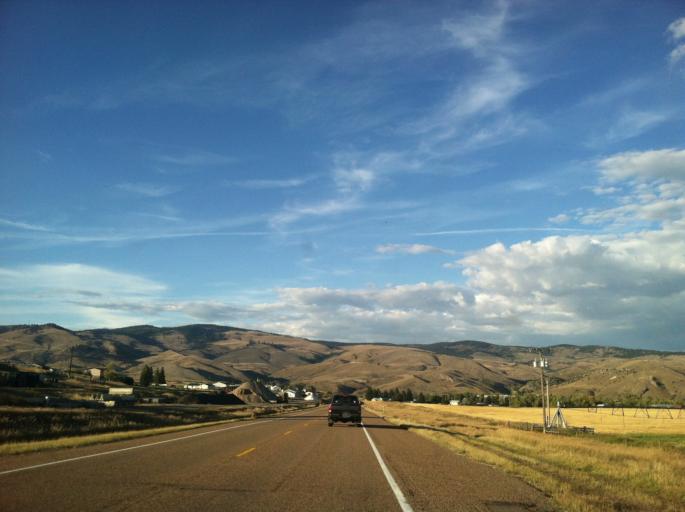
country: US
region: Montana
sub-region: Granite County
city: Philipsburg
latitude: 46.6520
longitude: -113.1614
